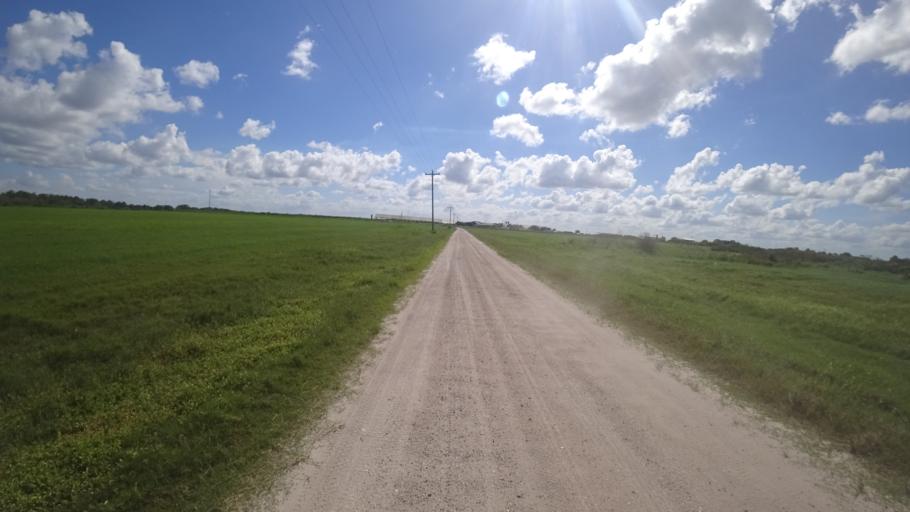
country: US
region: Florida
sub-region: DeSoto County
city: Arcadia
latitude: 27.3177
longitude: -82.1249
